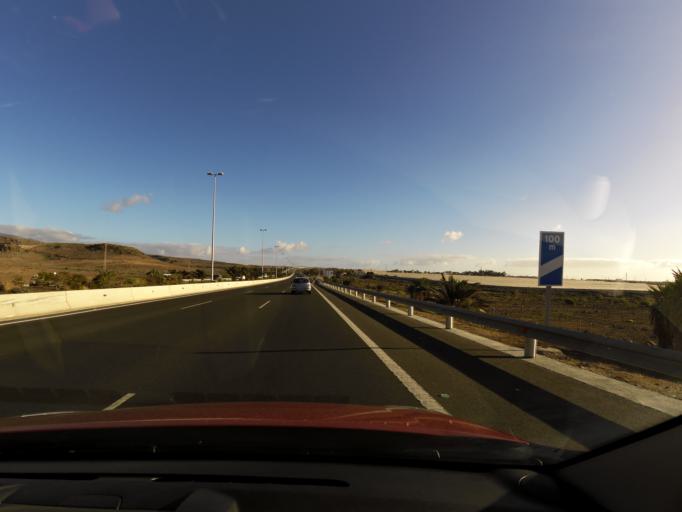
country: ES
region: Canary Islands
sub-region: Provincia de Las Palmas
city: Cruce de Arinaga
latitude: 27.8012
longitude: -15.4856
